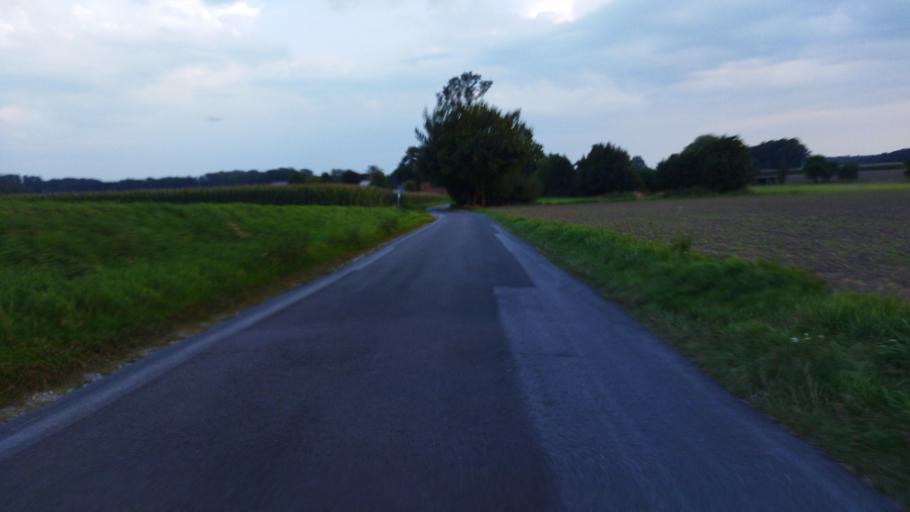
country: DE
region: Lower Saxony
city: Bad Iburg
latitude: 52.1368
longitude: 8.0540
